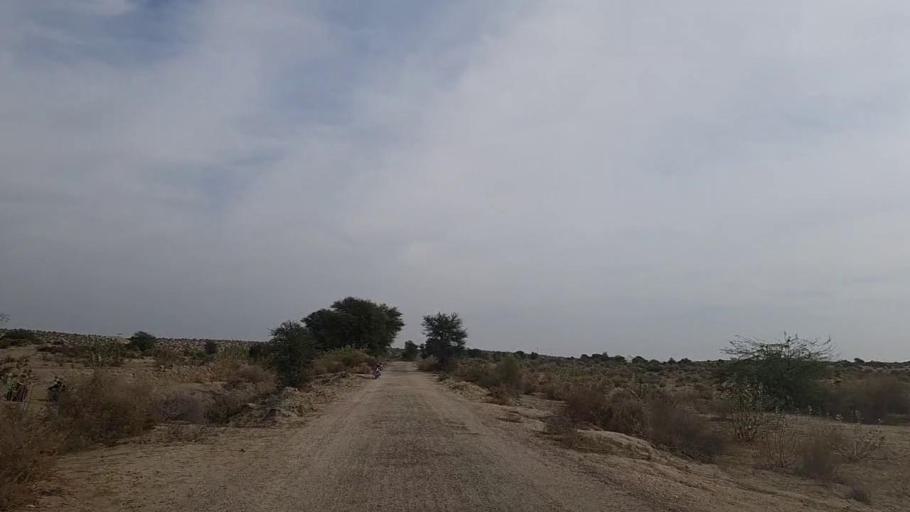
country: PK
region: Sindh
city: Jam Sahib
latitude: 26.4460
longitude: 68.6191
